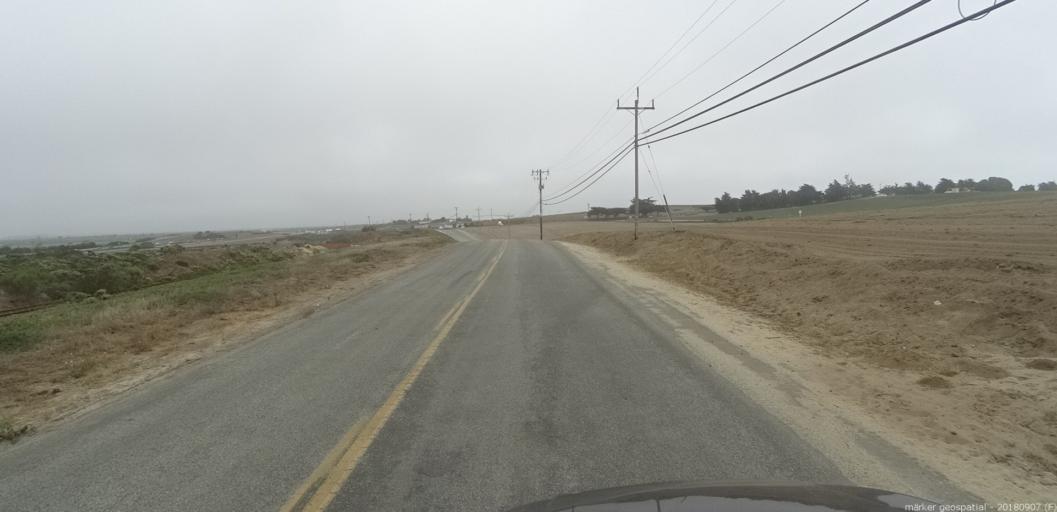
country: US
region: California
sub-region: Monterey County
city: Marina
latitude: 36.7187
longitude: -121.7901
